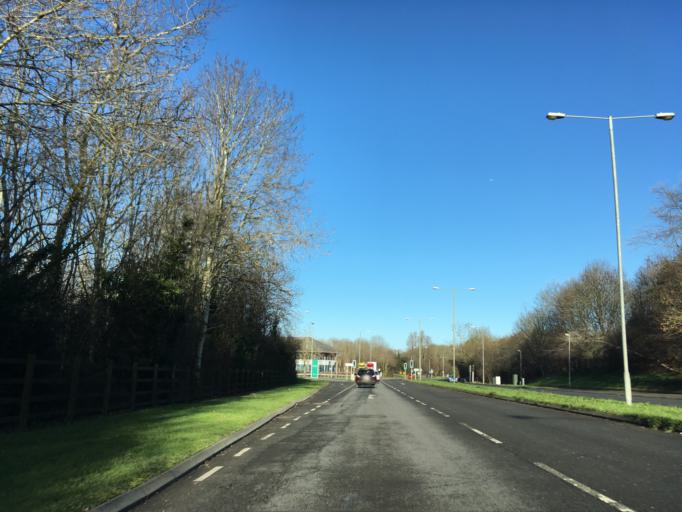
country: GB
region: England
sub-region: Wiltshire
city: Lydiard Tregoze
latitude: 51.5485
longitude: -1.8441
